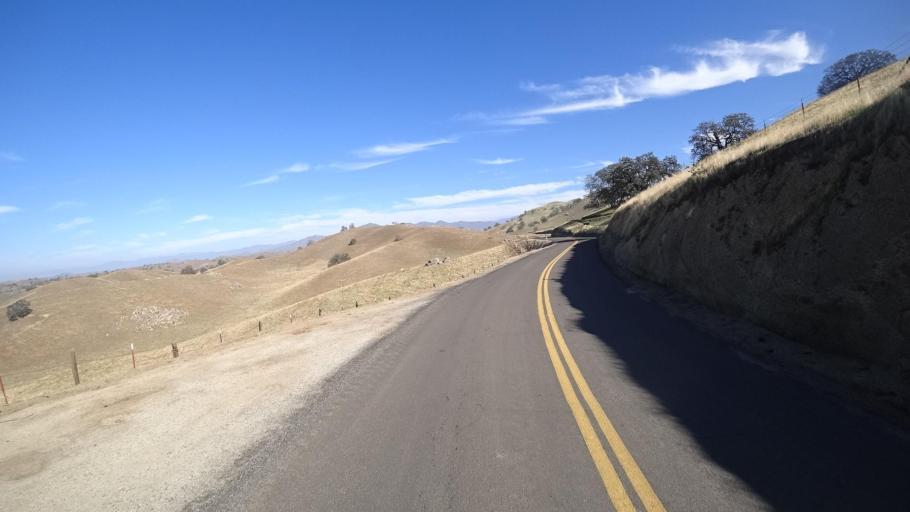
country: US
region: California
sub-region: Tulare County
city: Richgrove
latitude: 35.6886
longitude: -118.8788
